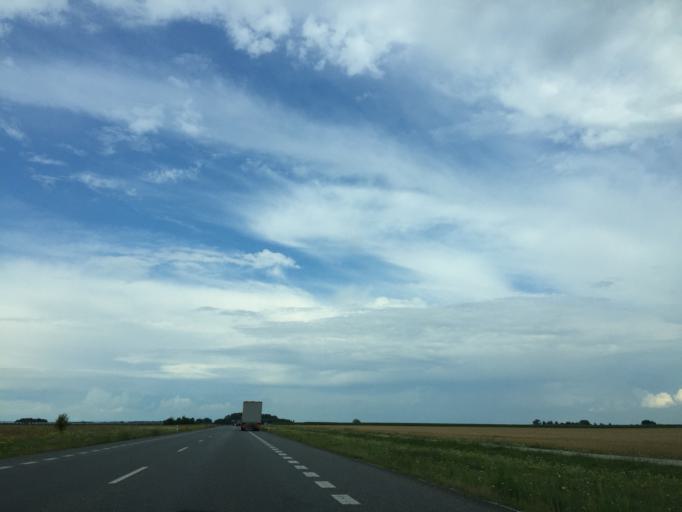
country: PL
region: Masovian Voivodeship
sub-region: Powiat grojecki
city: Chynow
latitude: 51.9058
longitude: 21.0348
